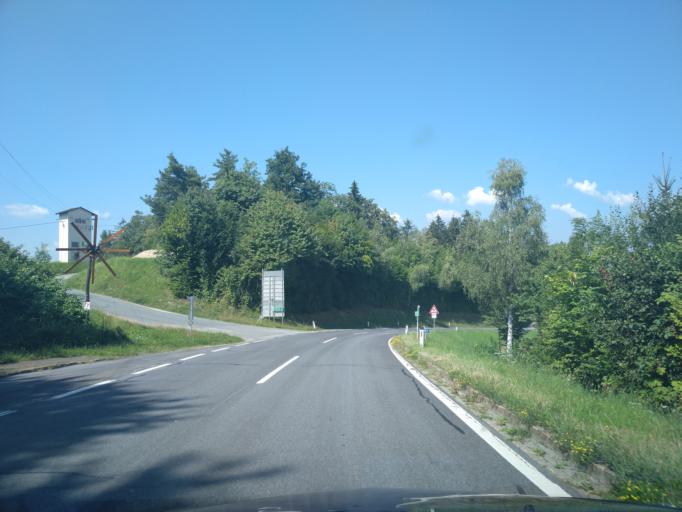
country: AT
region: Styria
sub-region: Politischer Bezirk Leibnitz
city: Leutschach
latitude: 46.6821
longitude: 15.4802
